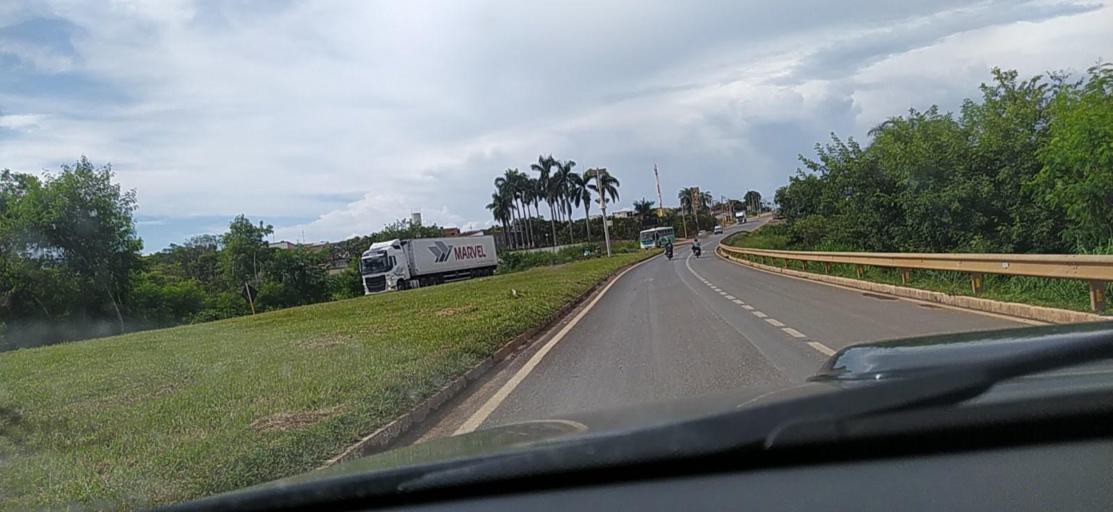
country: BR
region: Minas Gerais
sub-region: Montes Claros
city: Montes Claros
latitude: -16.7496
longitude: -43.8463
